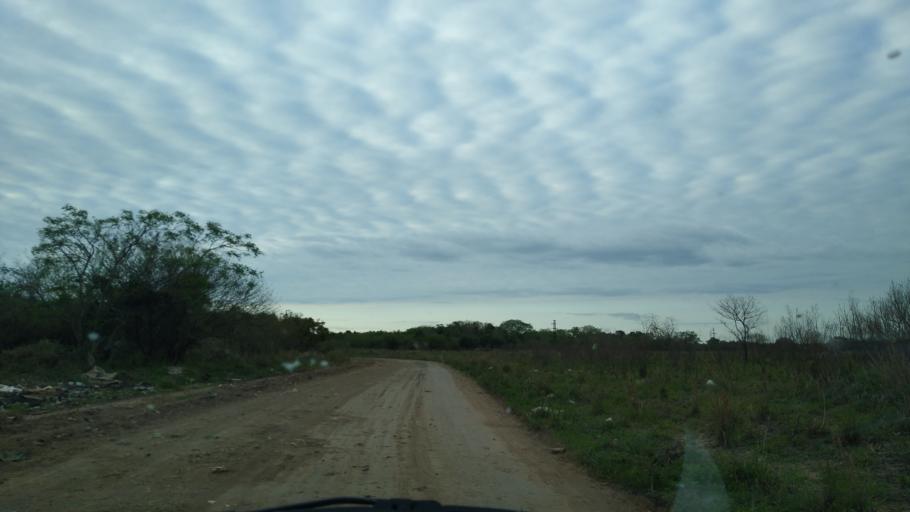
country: AR
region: Chaco
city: Fontana
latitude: -27.3928
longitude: -59.0502
